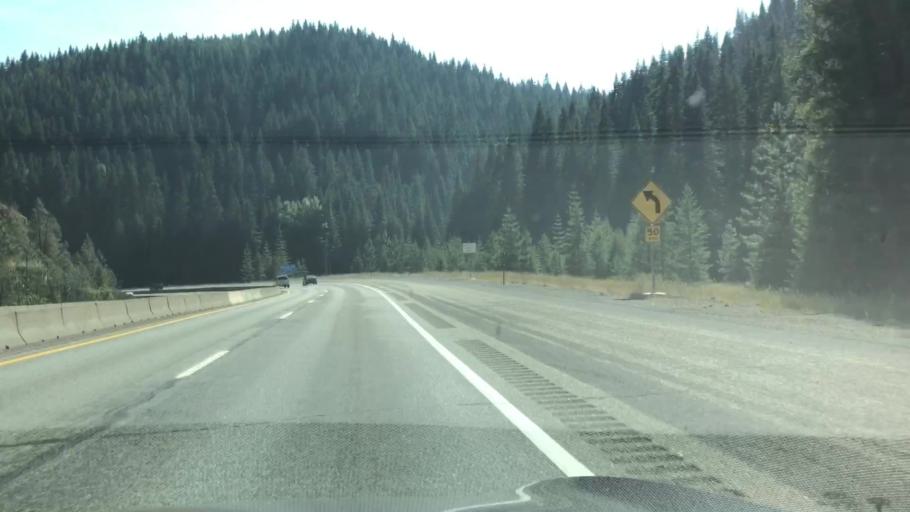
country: US
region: Idaho
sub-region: Shoshone County
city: Pinehurst
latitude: 47.5948
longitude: -116.4926
